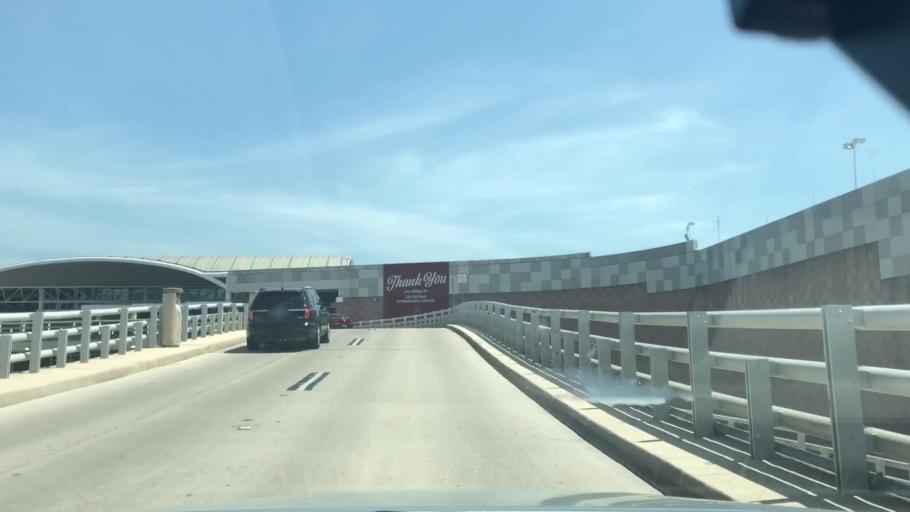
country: US
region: Texas
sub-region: Bexar County
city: Alamo Heights
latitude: 29.5254
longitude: -98.4727
